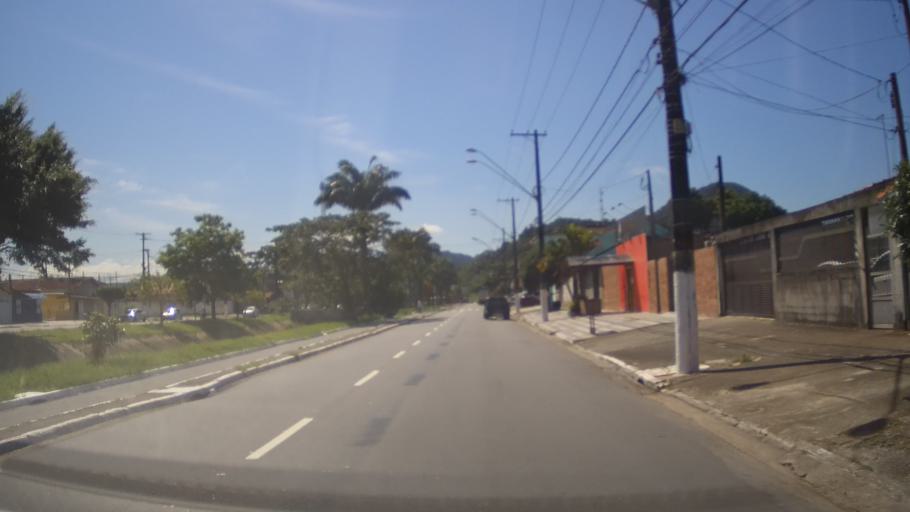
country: BR
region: Sao Paulo
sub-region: Praia Grande
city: Praia Grande
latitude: -23.9999
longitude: -46.4183
